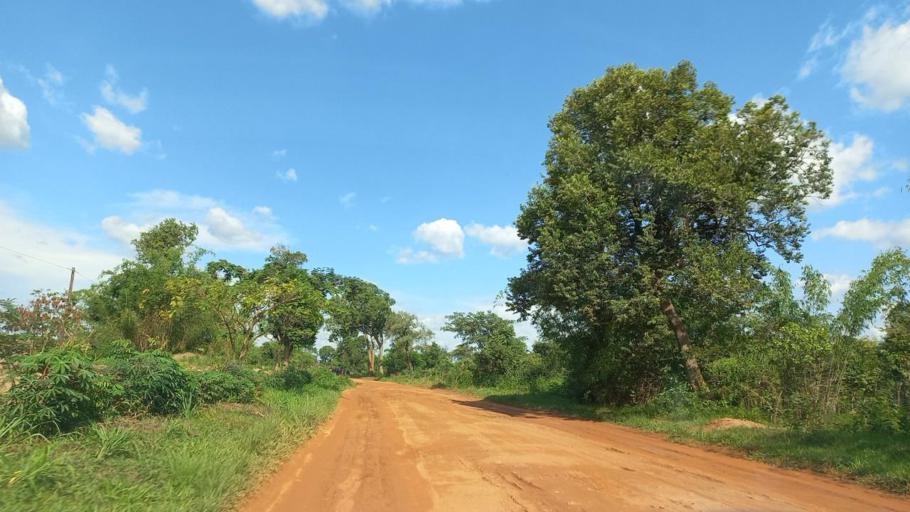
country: ZM
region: Copperbelt
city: Kitwe
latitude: -12.8646
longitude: 28.3747
